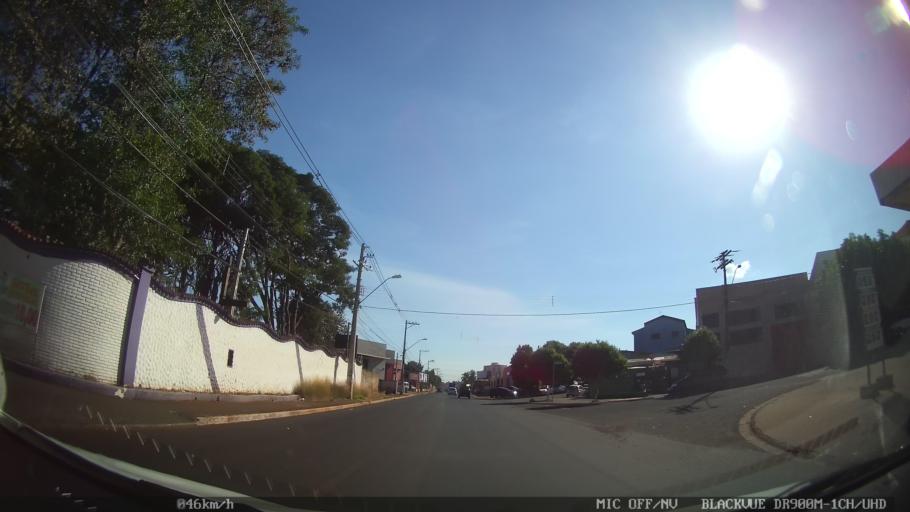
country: BR
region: Sao Paulo
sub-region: Ribeirao Preto
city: Ribeirao Preto
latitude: -21.1839
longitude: -47.7679
